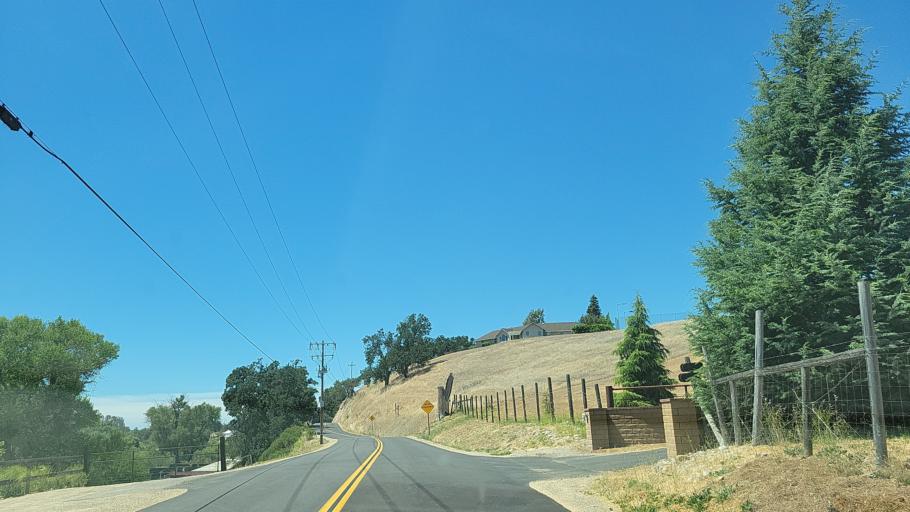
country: US
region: California
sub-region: San Luis Obispo County
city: Atascadero
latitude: 35.4888
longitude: -120.6382
